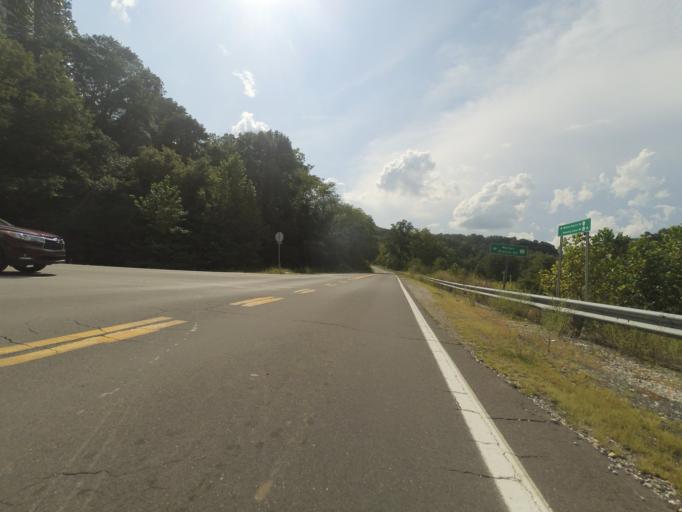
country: US
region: West Virginia
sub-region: Wayne County
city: Ceredo
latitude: 38.3719
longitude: -82.5466
